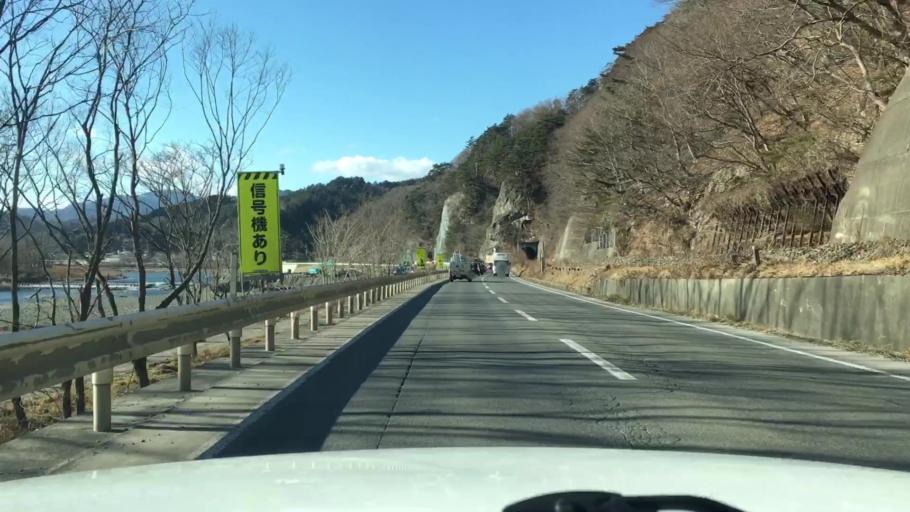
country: JP
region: Iwate
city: Miyako
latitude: 39.6315
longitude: 141.8711
